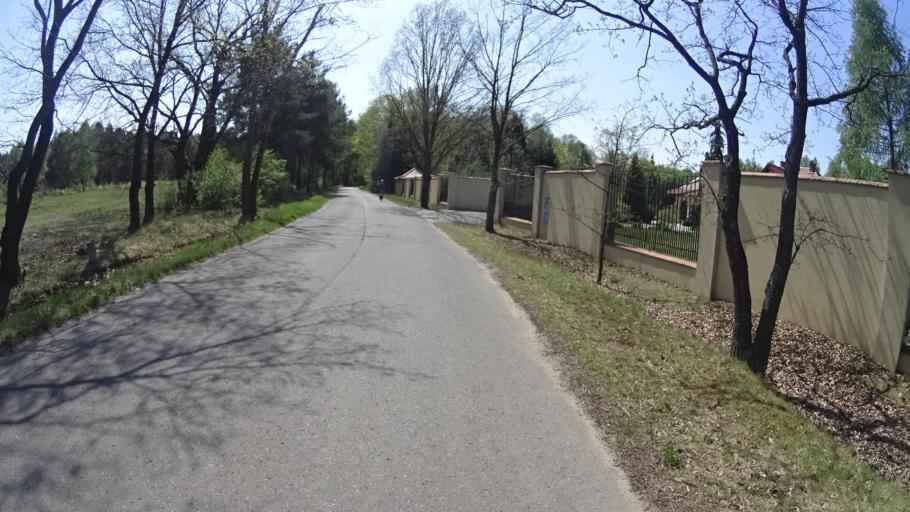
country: PL
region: Masovian Voivodeship
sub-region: Powiat warszawski zachodni
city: Truskaw
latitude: 52.2815
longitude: 20.7262
